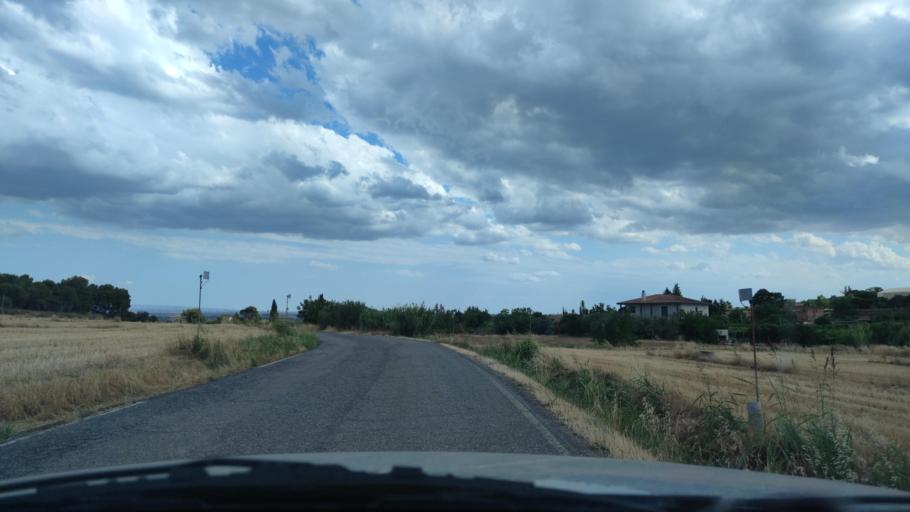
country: ES
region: Catalonia
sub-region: Provincia de Lleida
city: Lleida
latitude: 41.6046
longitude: 0.5854
